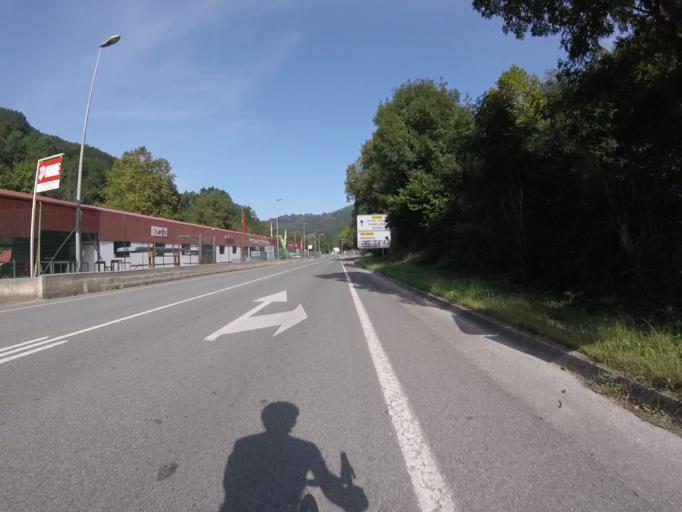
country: ES
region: Navarre
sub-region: Provincia de Navarra
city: Doneztebe
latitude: 43.1353
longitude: -1.5538
